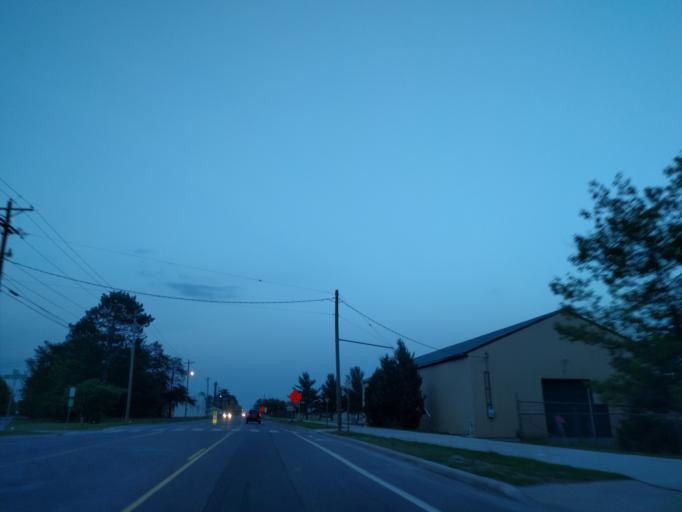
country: US
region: Michigan
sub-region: Marquette County
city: Trowbridge Park
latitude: 46.5639
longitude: -87.4158
